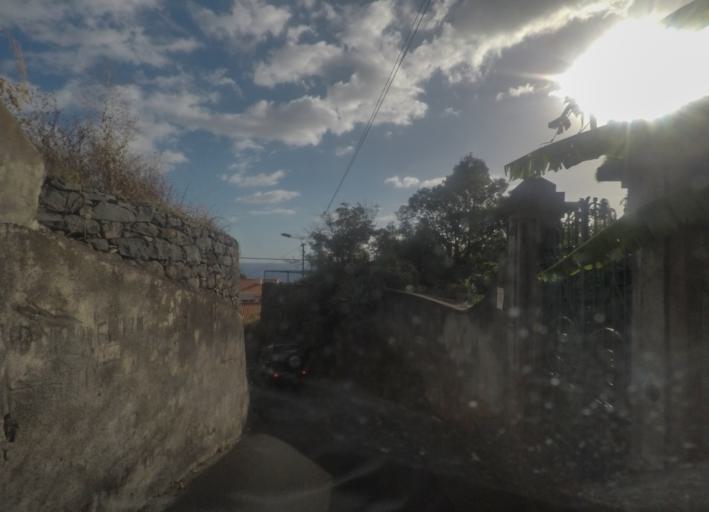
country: PT
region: Madeira
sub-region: Funchal
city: Nossa Senhora do Monte
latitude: 32.6537
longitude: -16.9029
